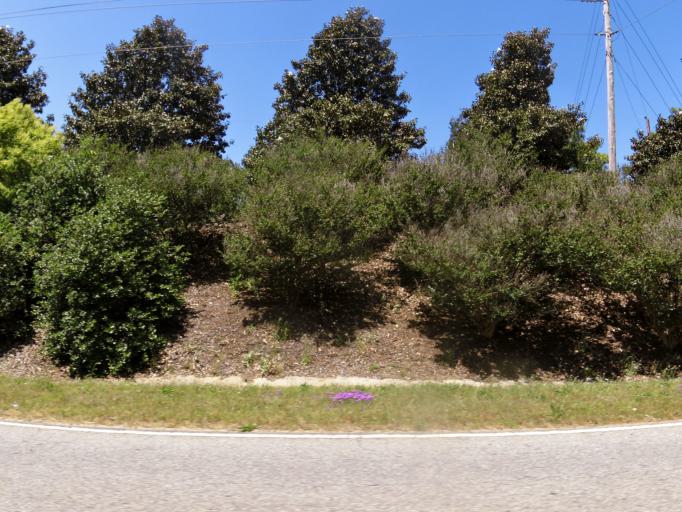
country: US
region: South Carolina
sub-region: Aiken County
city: Warrenville
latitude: 33.5628
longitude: -81.7725
